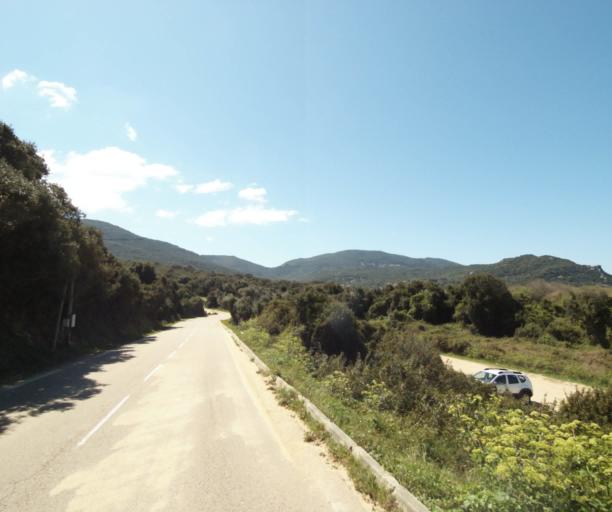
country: FR
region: Corsica
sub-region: Departement de la Corse-du-Sud
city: Propriano
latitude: 41.6505
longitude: 8.8800
